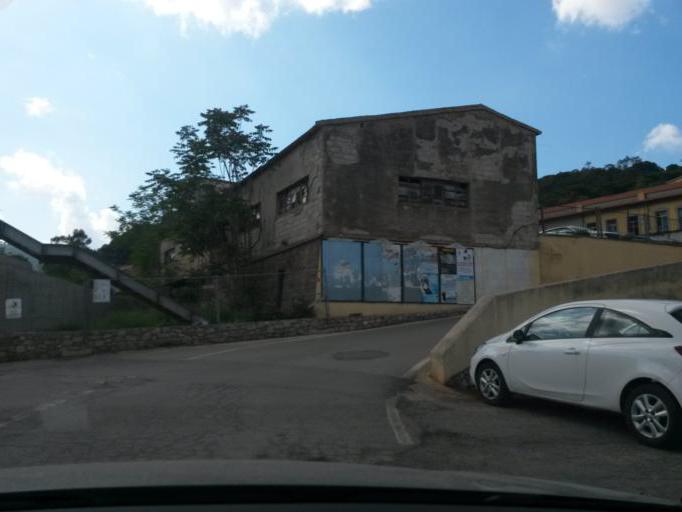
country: IT
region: Tuscany
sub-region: Provincia di Livorno
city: Rio Marina
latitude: 42.8141
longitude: 10.4254
